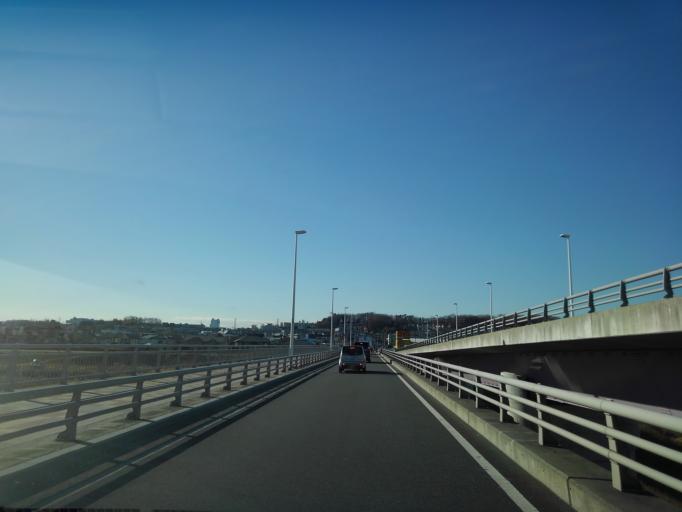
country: JP
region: Tokyo
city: Hino
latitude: 35.6926
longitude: 139.3728
